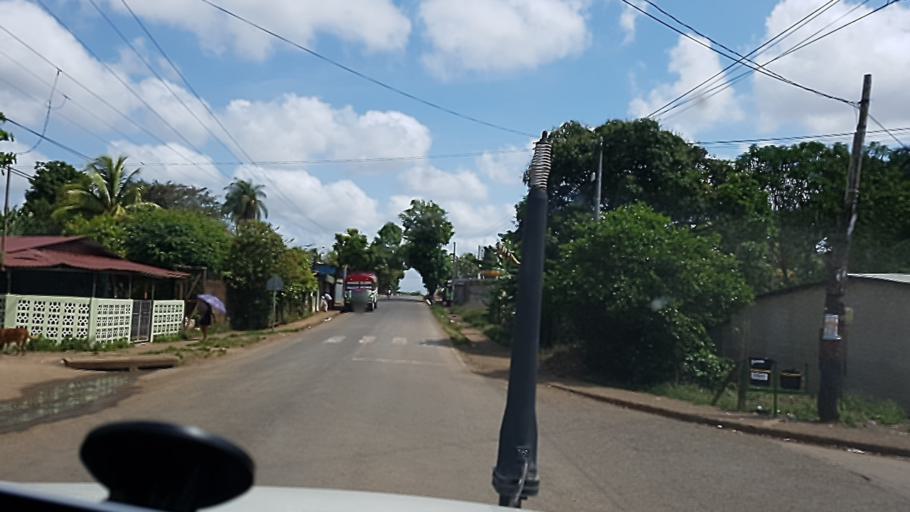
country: NI
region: Atlantico Sur
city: Nueva Guinea
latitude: 11.6873
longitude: -84.4610
